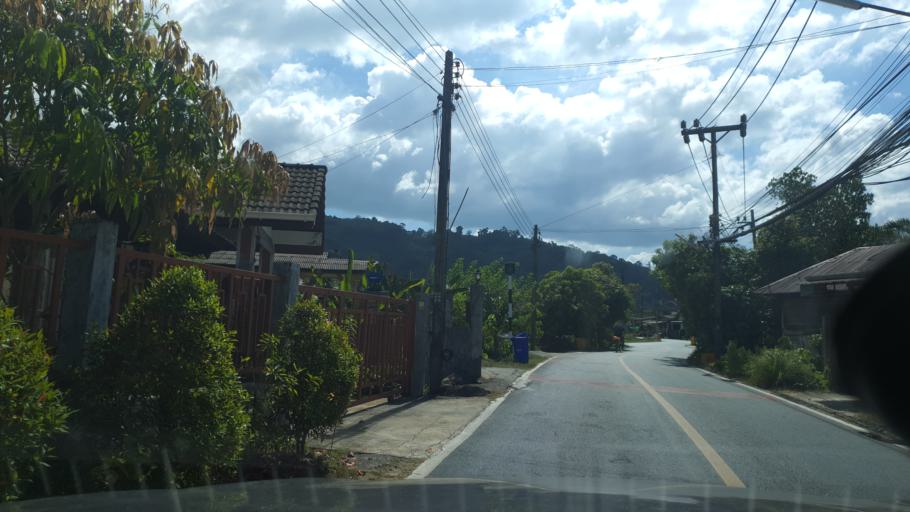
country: TH
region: Phuket
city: Thalang
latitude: 8.0728
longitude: 98.2972
